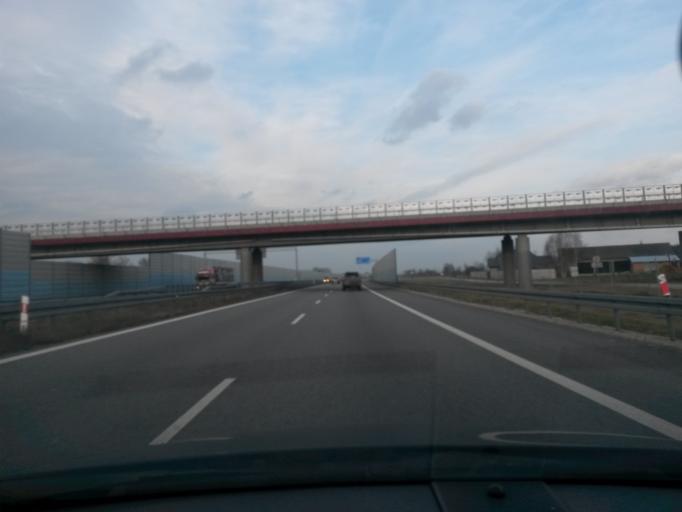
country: PL
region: Lodz Voivodeship
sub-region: powiat Lowicki
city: Lyszkowice
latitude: 51.9913
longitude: 19.9047
